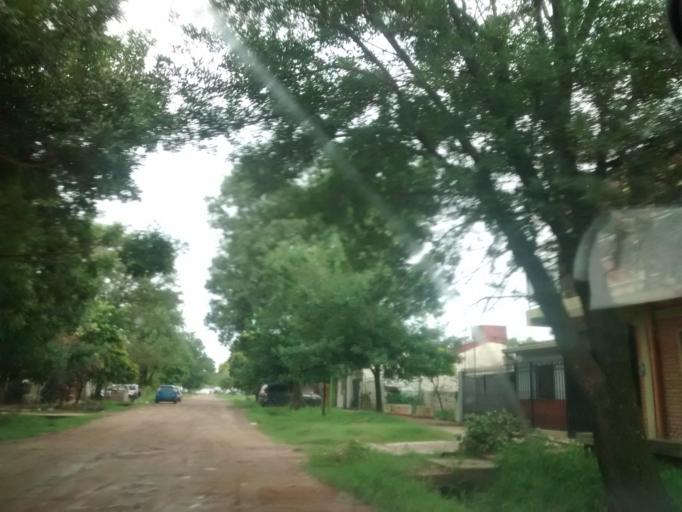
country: AR
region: Chaco
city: Resistencia
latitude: -27.4399
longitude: -58.9808
